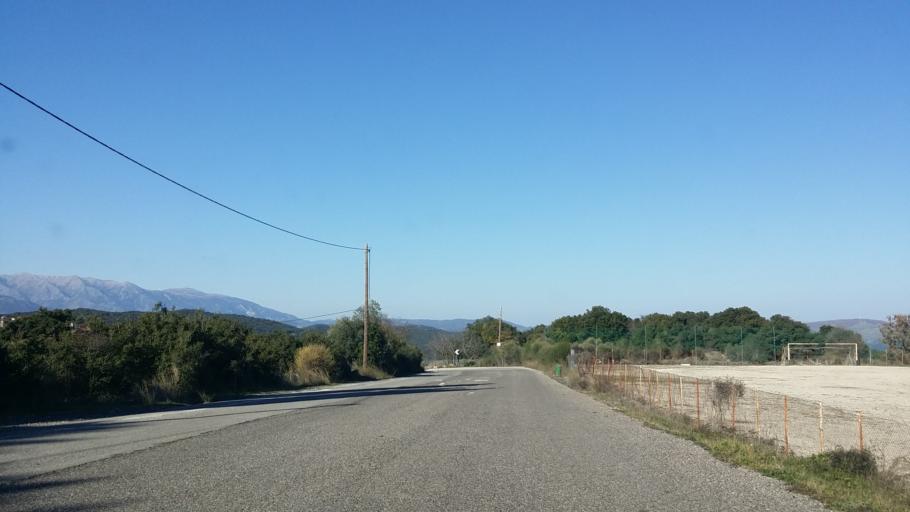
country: GR
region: West Greece
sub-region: Nomos Aitolias kai Akarnanias
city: Fitiai
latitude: 38.7065
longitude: 21.1829
